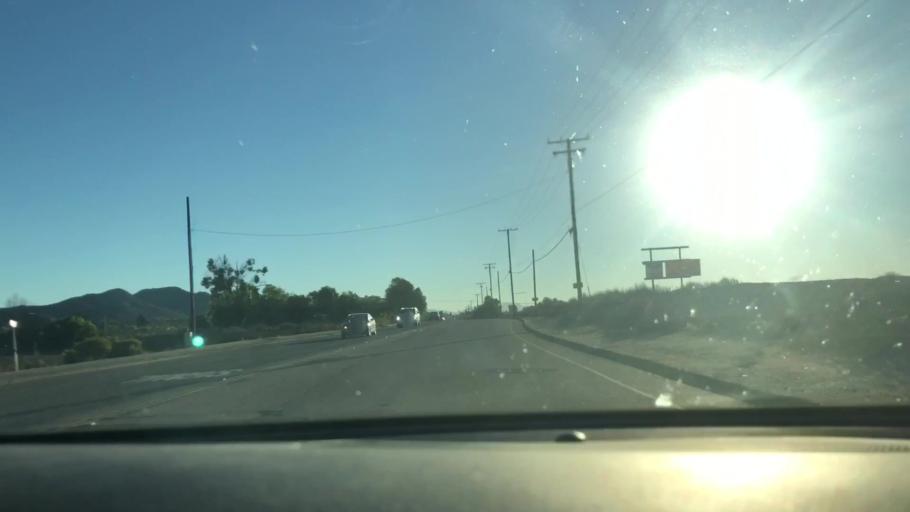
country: US
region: California
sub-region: Riverside County
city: Wildomar
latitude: 33.5977
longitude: -117.2351
